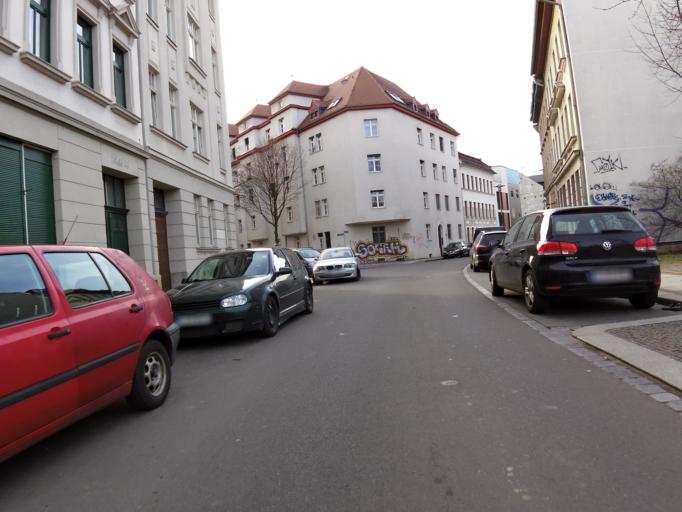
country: DE
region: Saxony
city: Leipzig
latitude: 51.3427
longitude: 12.4042
